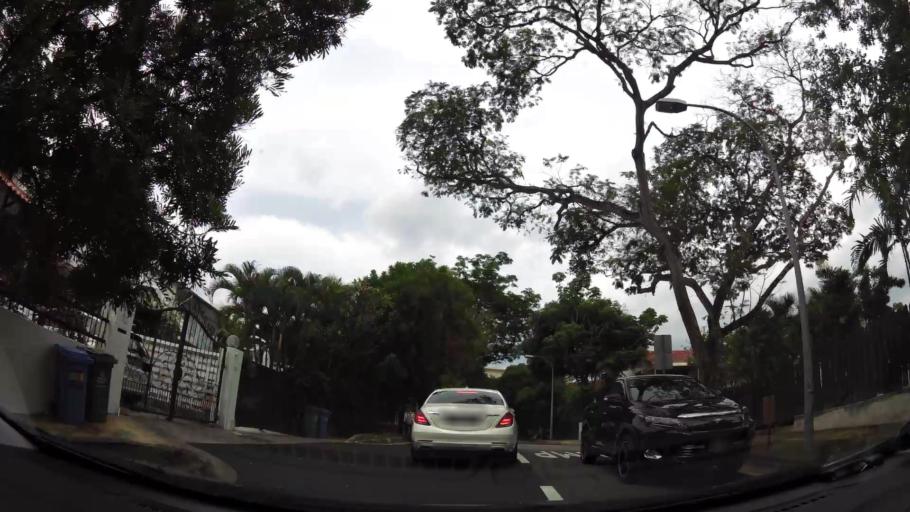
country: SG
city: Singapore
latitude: 1.3146
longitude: 103.7832
